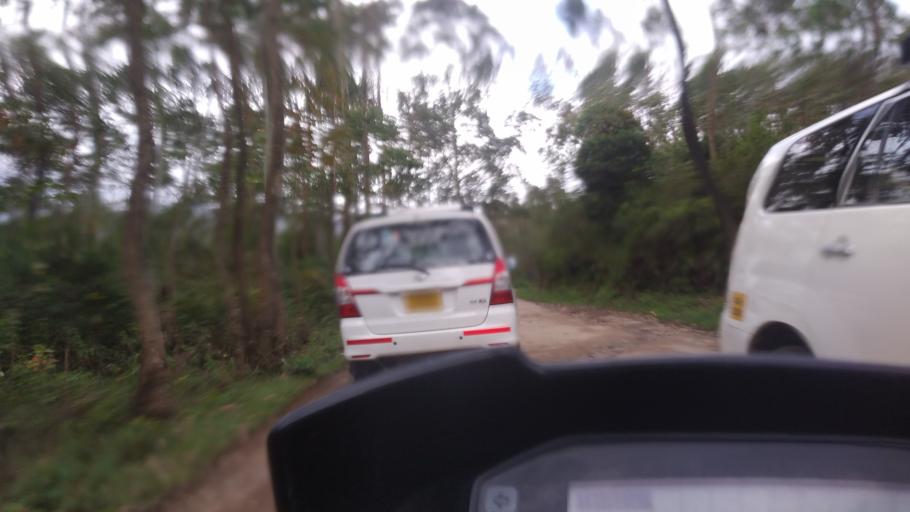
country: IN
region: Kerala
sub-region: Idukki
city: Munnar
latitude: 10.0574
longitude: 77.1084
